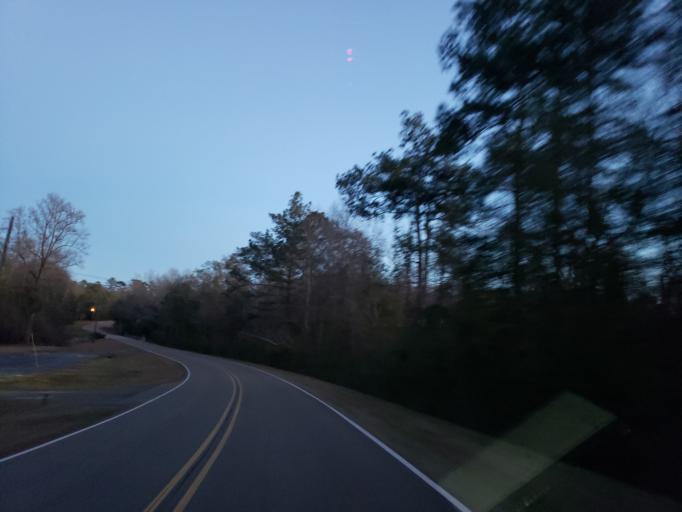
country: US
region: Mississippi
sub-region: Forrest County
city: Rawls Springs
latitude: 31.4284
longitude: -89.3580
